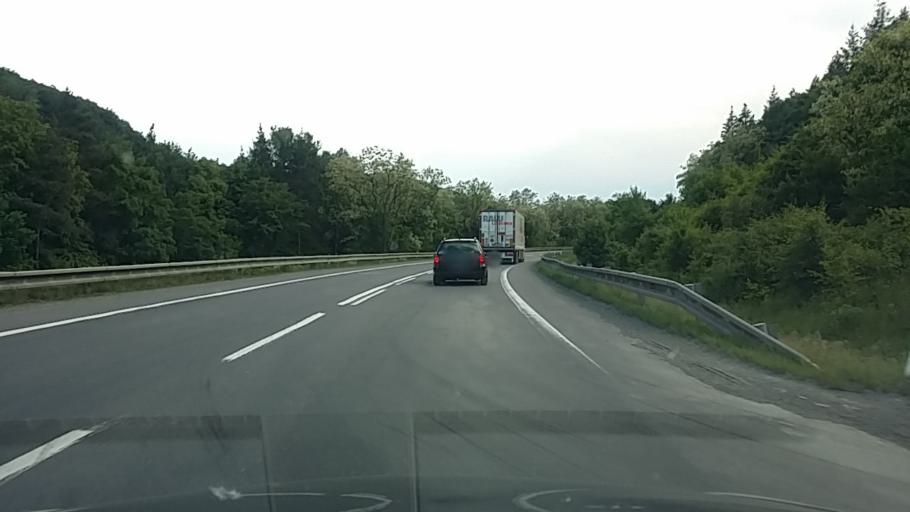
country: SK
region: Banskobystricky
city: Krupina
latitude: 48.3945
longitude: 19.0864
